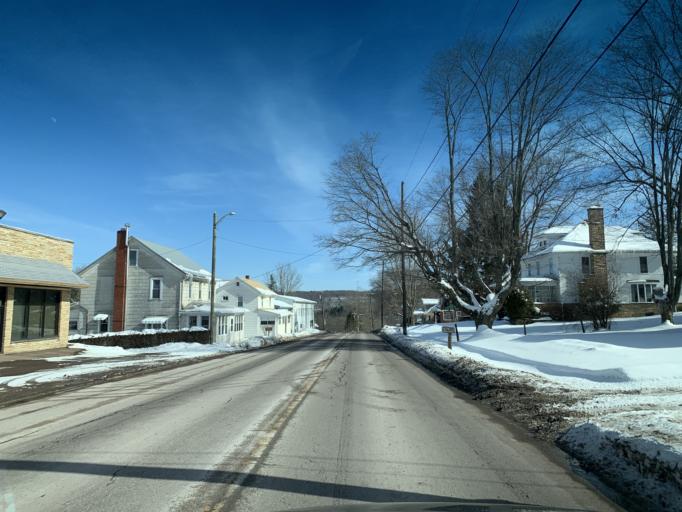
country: US
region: Pennsylvania
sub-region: Somerset County
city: Meyersdale
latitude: 39.6958
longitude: -79.1515
